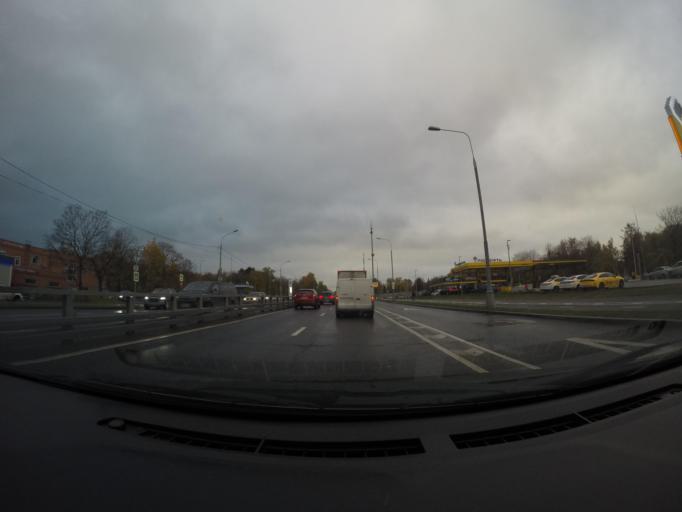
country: RU
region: Moskovskaya
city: Kastanayevo
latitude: 55.7257
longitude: 37.4959
